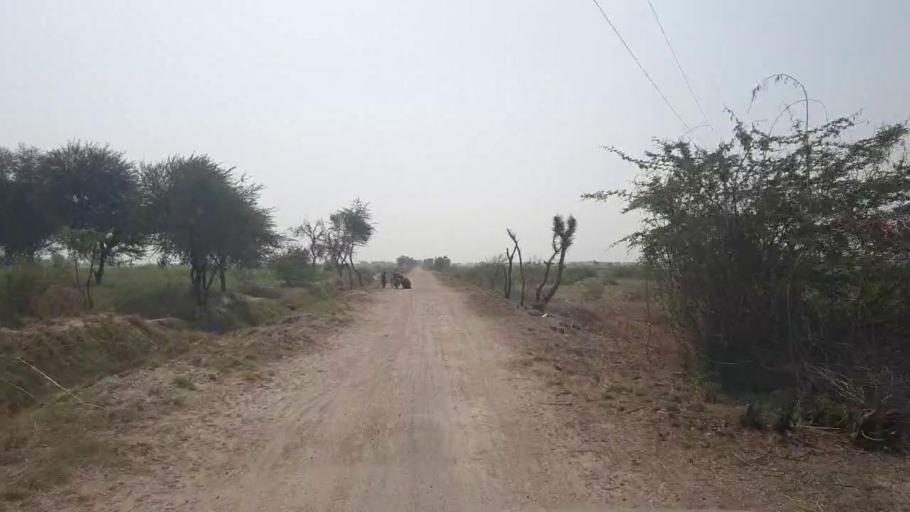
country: PK
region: Sindh
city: Dhoro Naro
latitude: 25.4475
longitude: 69.6251
